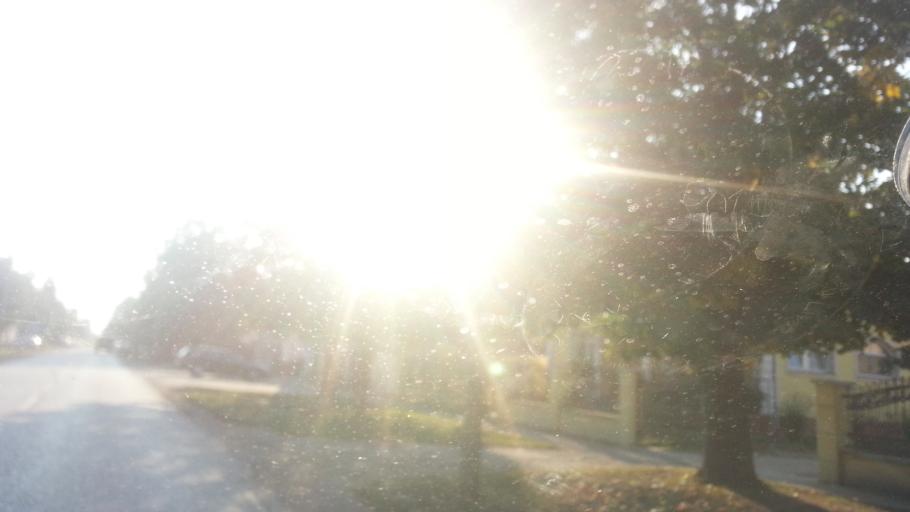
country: RS
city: Novi Slankamen
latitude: 45.1235
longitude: 20.2359
